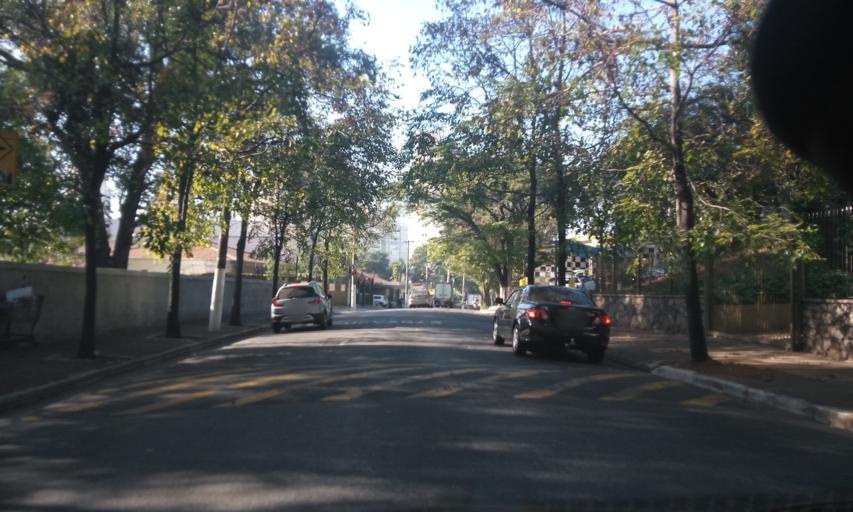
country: BR
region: Sao Paulo
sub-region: Sao Paulo
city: Sao Paulo
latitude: -23.5934
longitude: -46.6339
